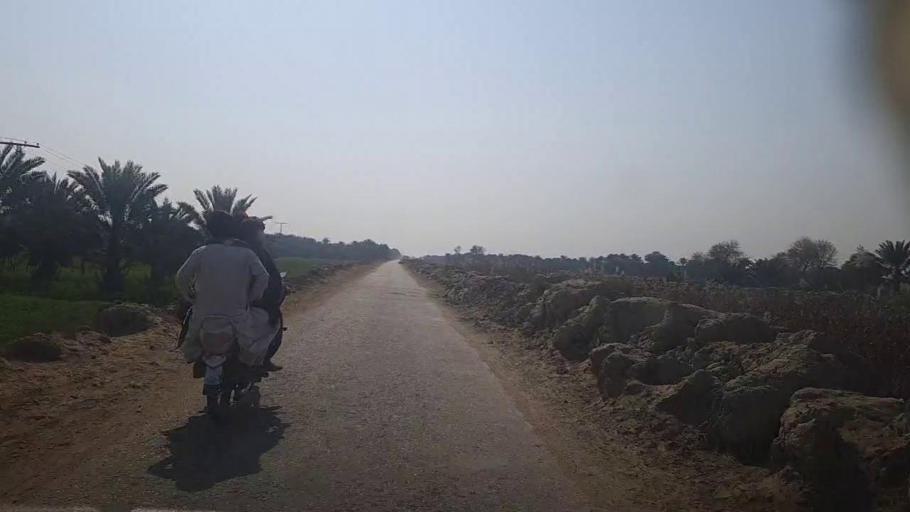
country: PK
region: Sindh
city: Khairpur
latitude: 27.4571
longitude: 68.8147
